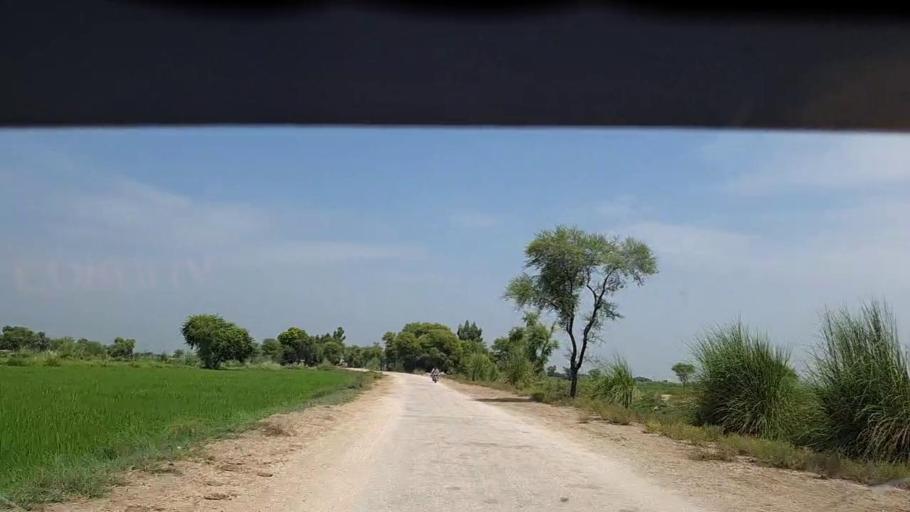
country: PK
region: Sindh
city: Shikarpur
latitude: 28.0660
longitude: 68.7053
